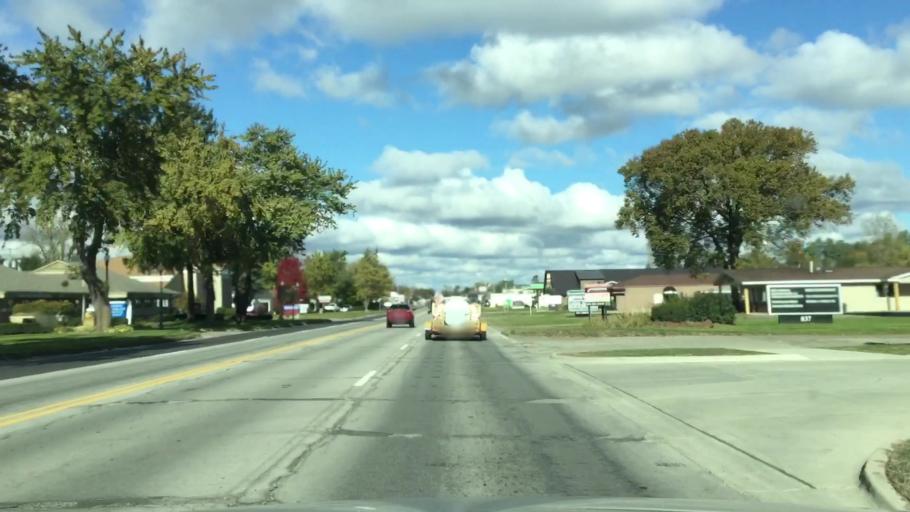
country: US
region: Michigan
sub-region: Oakland County
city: Oxford
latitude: 42.8128
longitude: -83.2539
